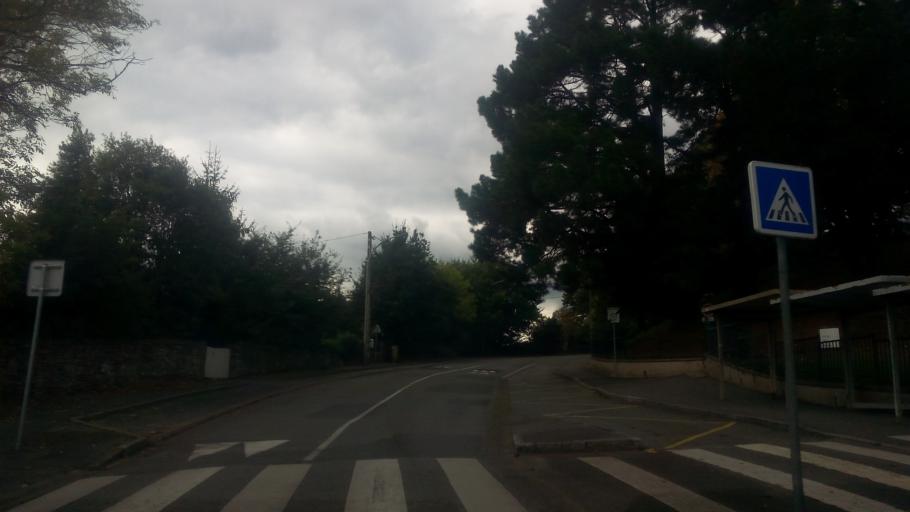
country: FR
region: Brittany
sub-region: Departement d'Ille-et-Vilaine
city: Redon
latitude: 47.6552
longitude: -2.0761
